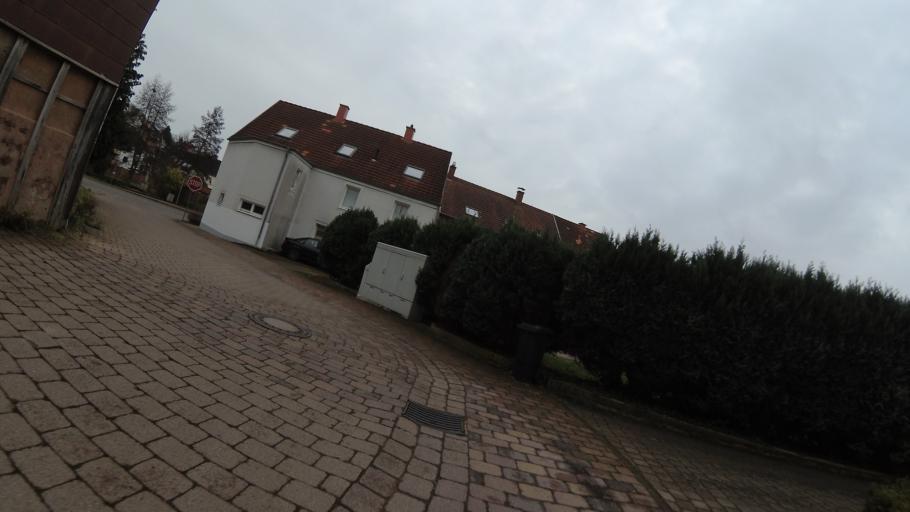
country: DE
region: Rheinland-Pfalz
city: Breitenbach
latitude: 49.4349
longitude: 7.2720
